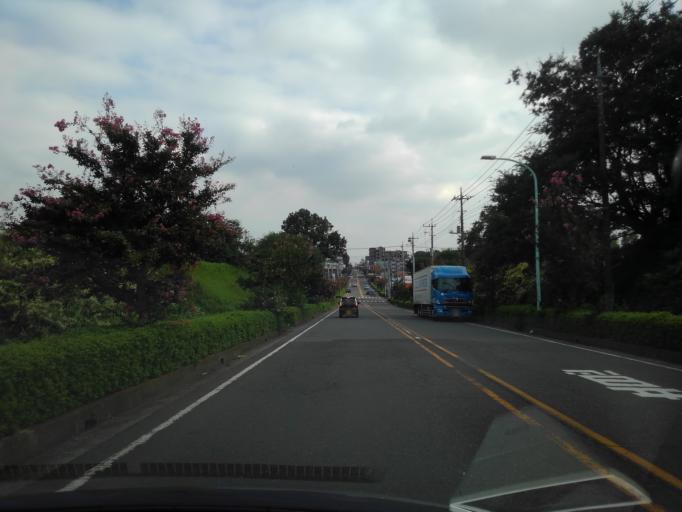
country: JP
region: Saitama
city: Tokorozawa
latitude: 35.8024
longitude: 139.5084
